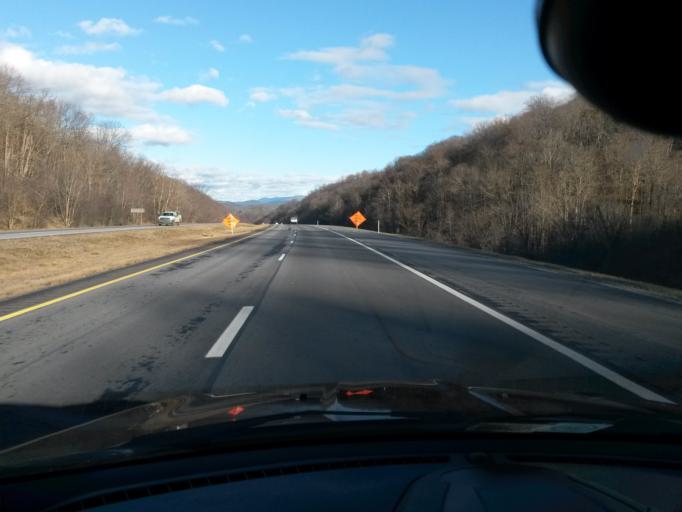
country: US
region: Virginia
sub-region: Giles County
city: Narrows
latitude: 37.3595
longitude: -80.8837
